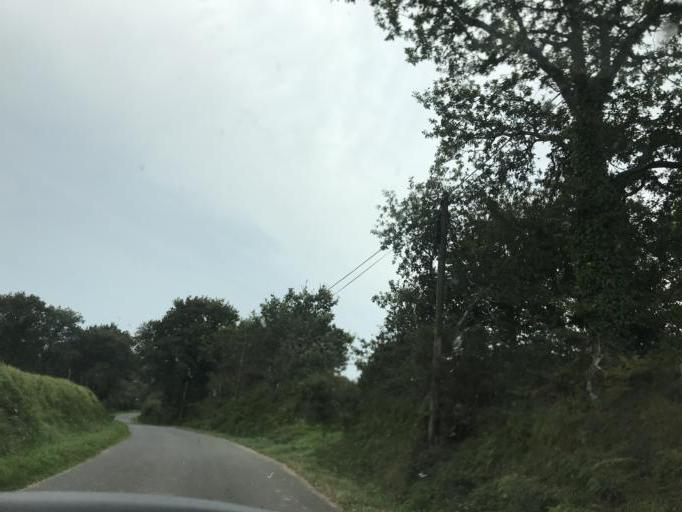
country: FR
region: Brittany
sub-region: Departement du Finistere
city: Plouneour-Menez
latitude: 48.3632
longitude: -3.8665
